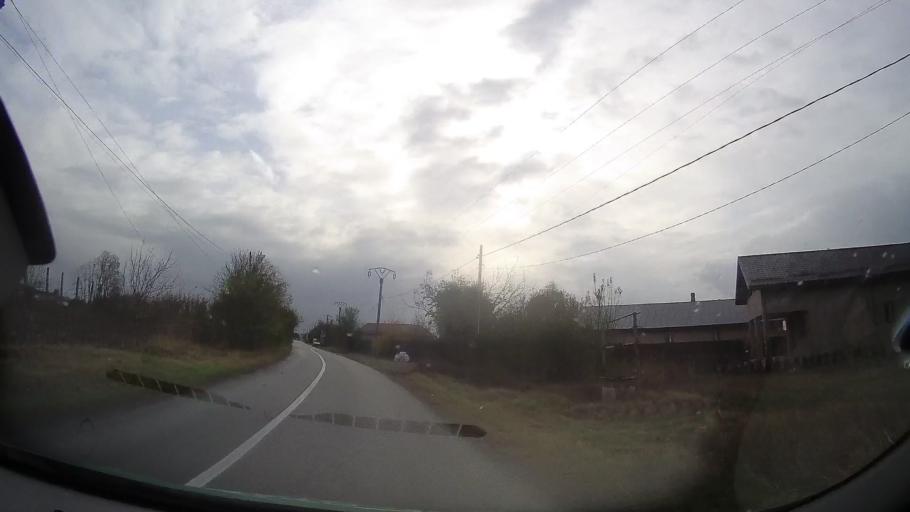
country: RO
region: Ialomita
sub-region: Comuna Fierbinti-Targ
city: Fierbintii de Jos
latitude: 44.7000
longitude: 26.3936
